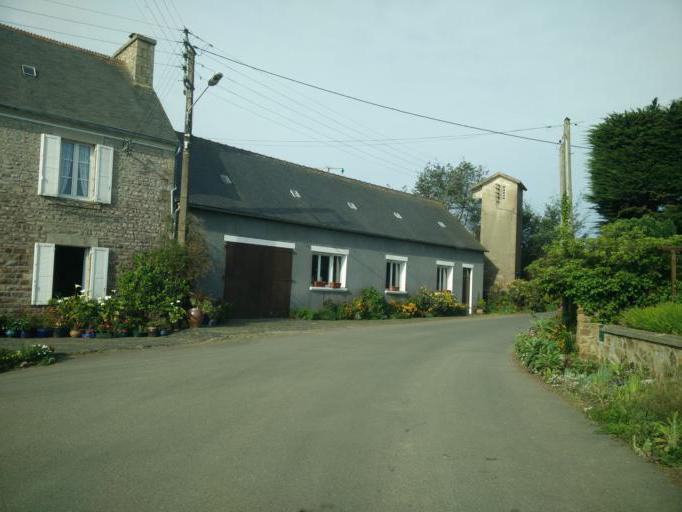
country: FR
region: Brittany
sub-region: Departement des Cotes-d'Armor
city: Lezardrieux
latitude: 48.8267
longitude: -3.0891
